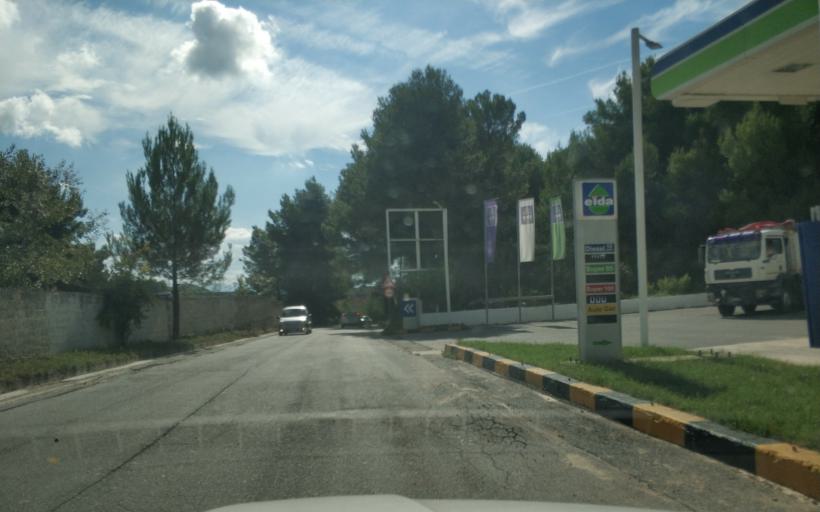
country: AL
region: Durres
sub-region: Rrethi i Krujes
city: Kruje
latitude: 41.4996
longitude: 19.7770
